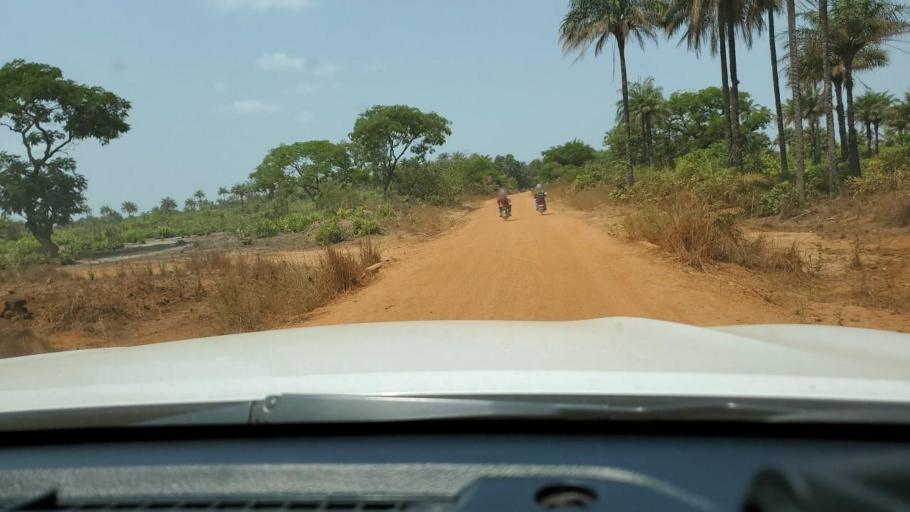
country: GN
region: Boke
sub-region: Boffa
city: Boffa
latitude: 10.0908
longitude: -13.8613
